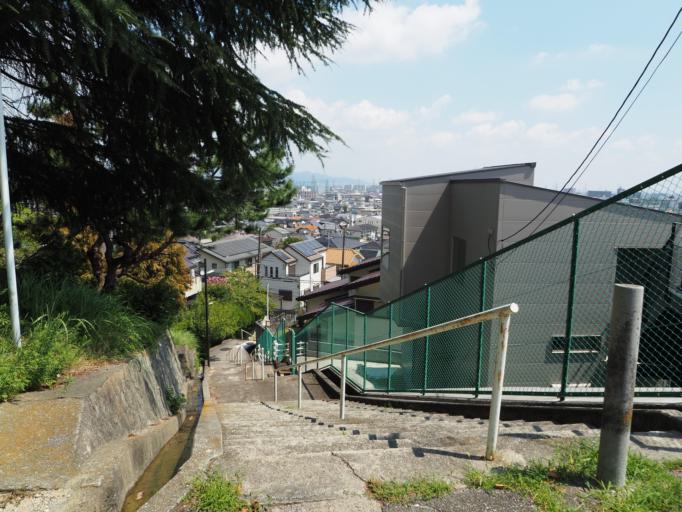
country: JP
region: Hyogo
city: Takarazuka
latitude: 34.7837
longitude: 135.3521
